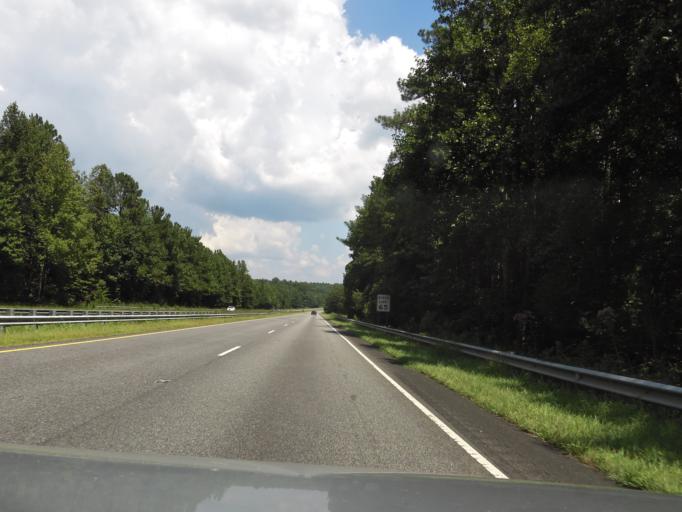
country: US
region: North Carolina
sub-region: Polk County
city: Columbus
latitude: 35.2633
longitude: -82.1735
